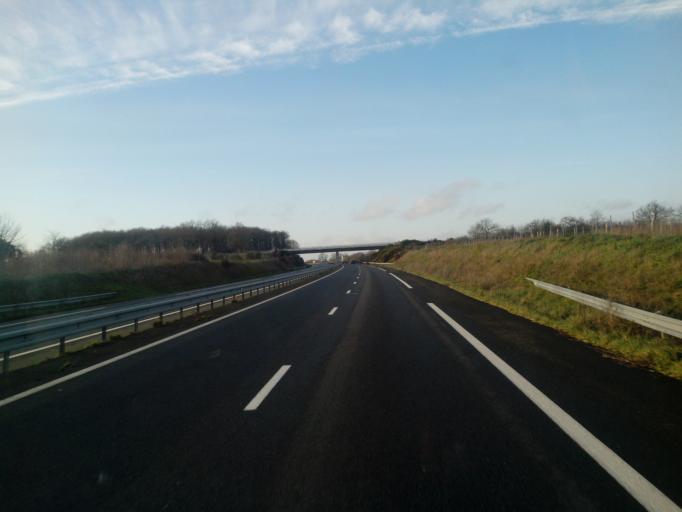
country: FR
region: Poitou-Charentes
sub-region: Departement des Deux-Sevres
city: Combrand
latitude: 46.9223
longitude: -0.7010
